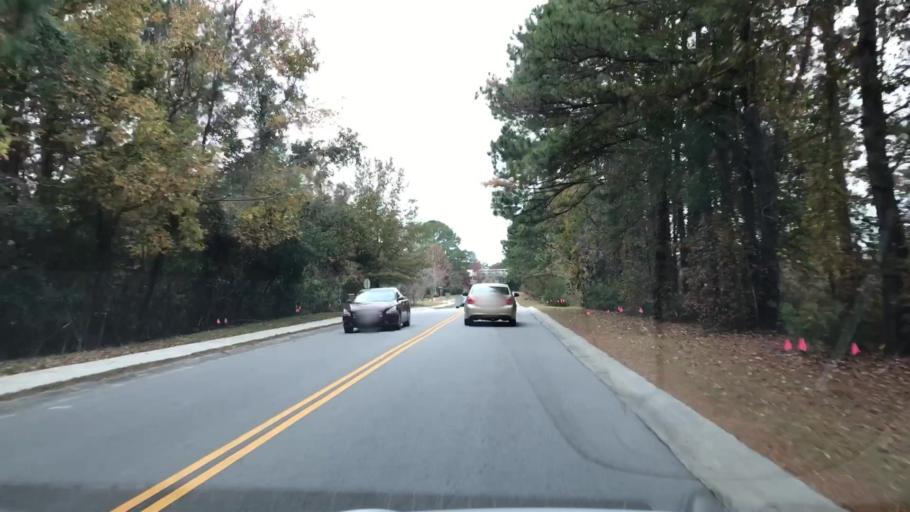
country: US
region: South Carolina
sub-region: Charleston County
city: Mount Pleasant
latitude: 32.8437
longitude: -79.8712
